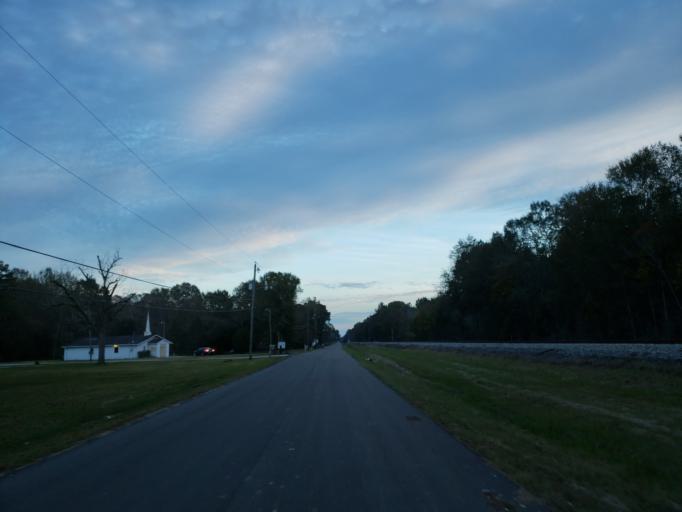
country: US
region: Mississippi
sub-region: Forrest County
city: Hattiesburg
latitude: 31.2795
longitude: -89.2564
